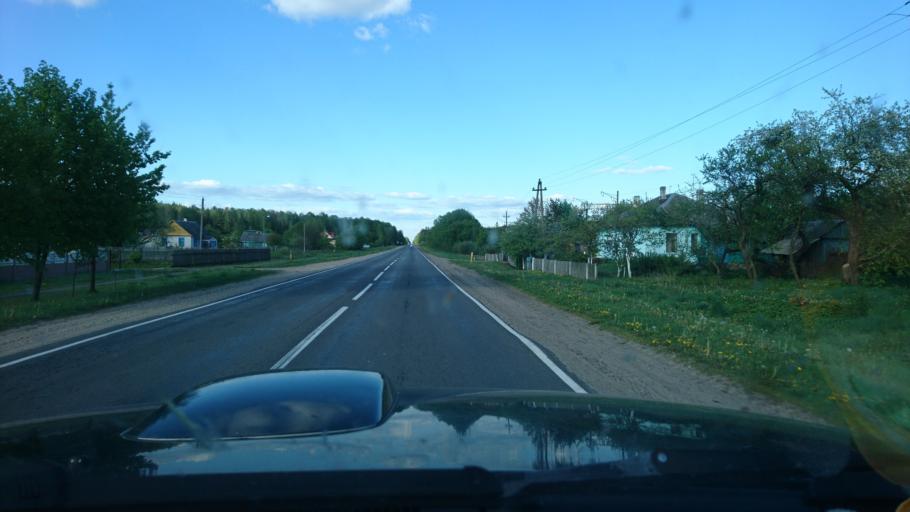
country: BY
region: Brest
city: Nyakhachava
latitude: 52.6519
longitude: 25.2217
